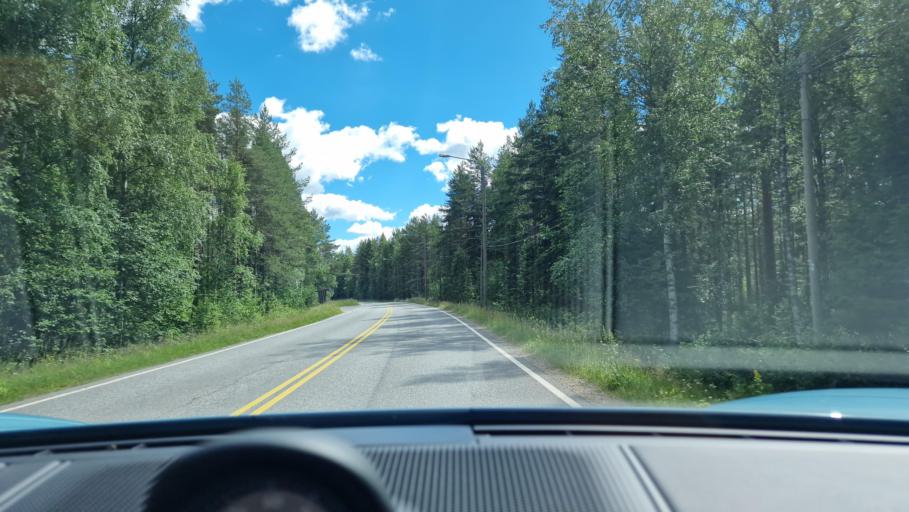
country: FI
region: Southern Ostrobothnia
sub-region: Jaerviseutu
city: Soini
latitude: 62.8365
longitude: 24.3308
